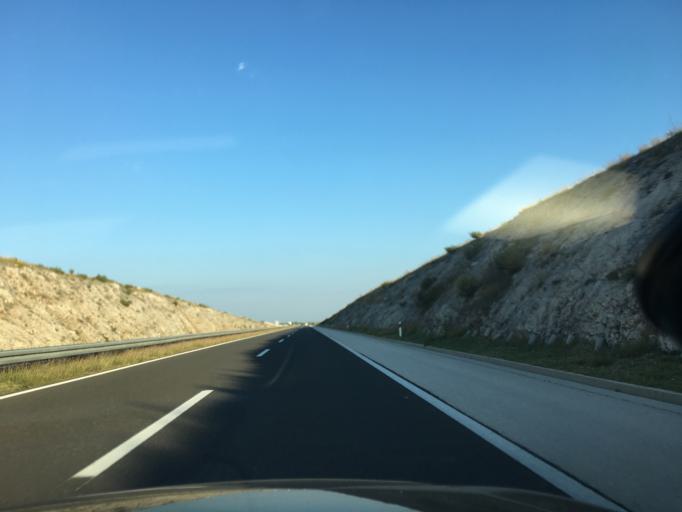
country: HR
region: Zadarska
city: Polaca
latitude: 44.0756
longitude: 15.5143
